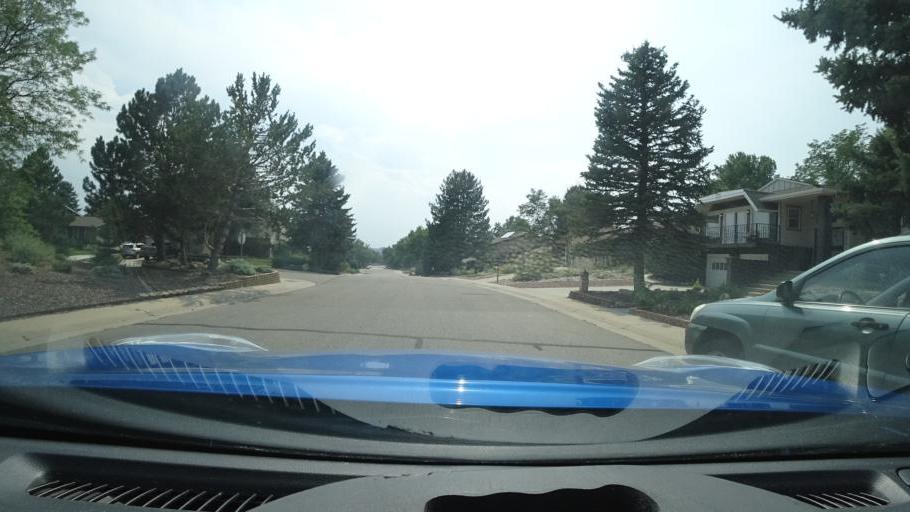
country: US
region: Colorado
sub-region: Adams County
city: Aurora
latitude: 39.6709
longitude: -104.8570
